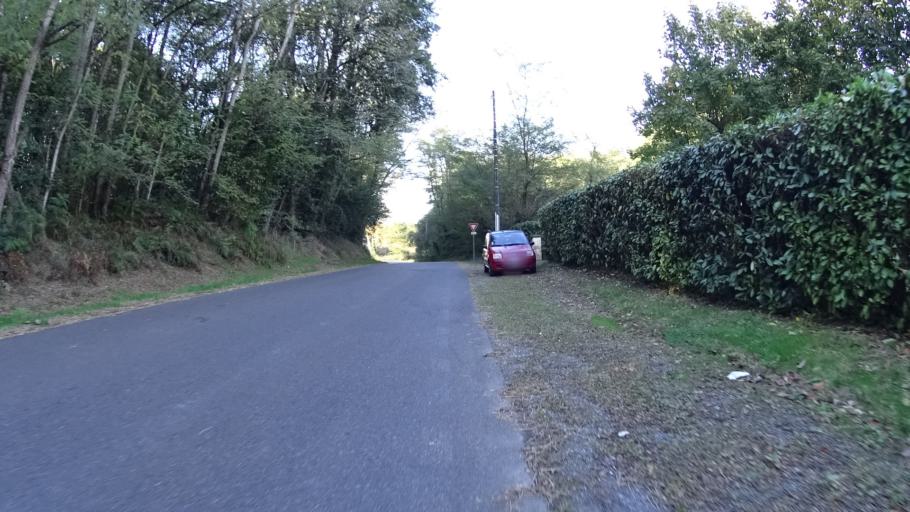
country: FR
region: Aquitaine
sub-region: Departement des Landes
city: Saint-Paul-les-Dax
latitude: 43.7371
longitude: -1.0436
